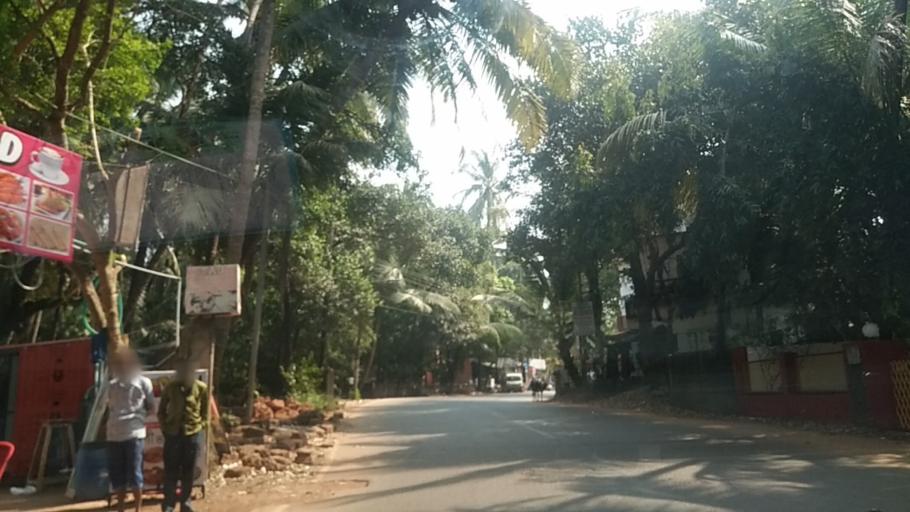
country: IN
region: Goa
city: Calangute
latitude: 15.5522
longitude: 73.7640
